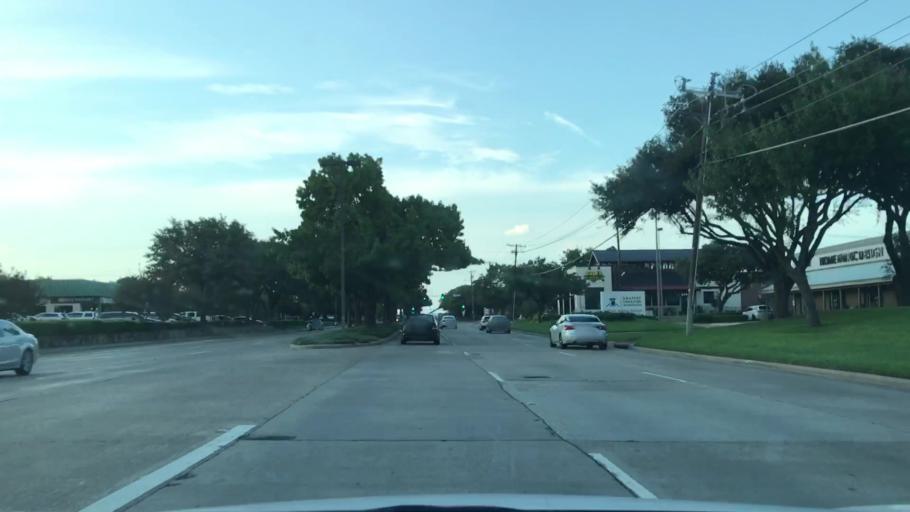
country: US
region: Texas
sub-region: Dallas County
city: Addison
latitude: 32.9503
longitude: -96.8388
